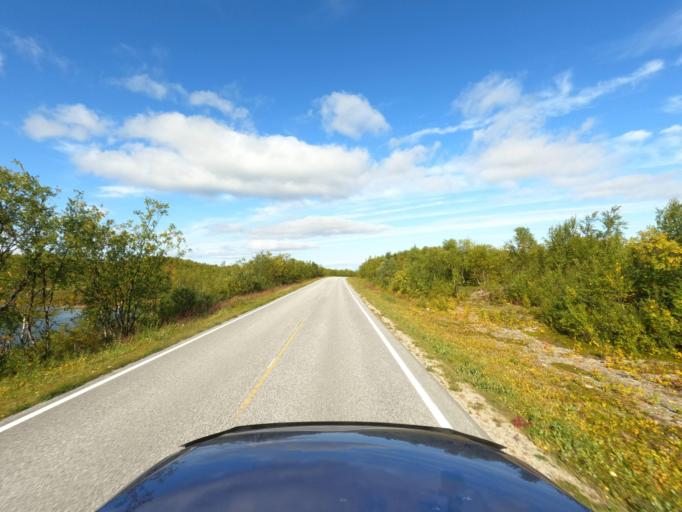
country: NO
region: Finnmark Fylke
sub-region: Karasjok
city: Karasjohka
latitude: 69.6009
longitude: 25.3281
